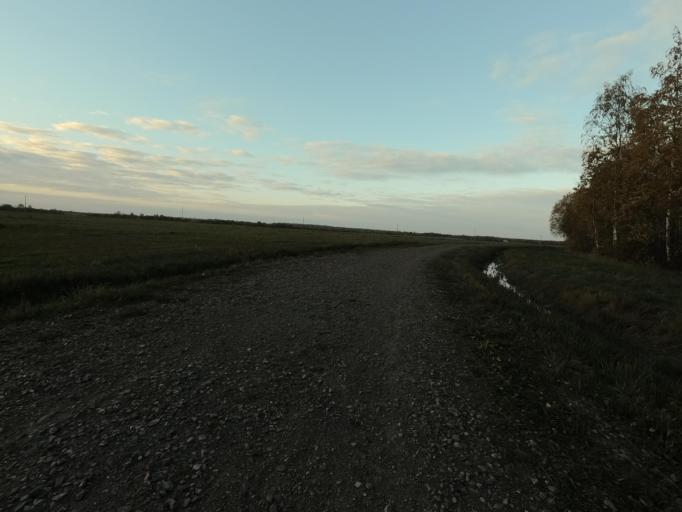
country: RU
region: Leningrad
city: Mga
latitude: 59.7833
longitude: 31.1959
